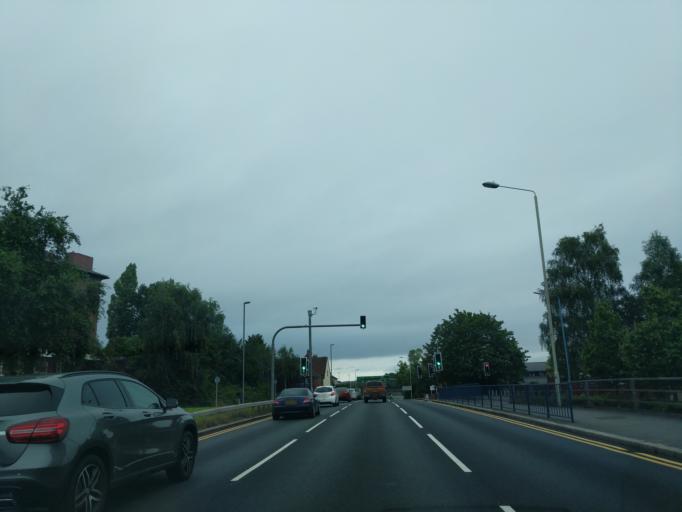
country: GB
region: England
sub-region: Dudley
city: Stourbridge
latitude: 52.4578
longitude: -2.1496
